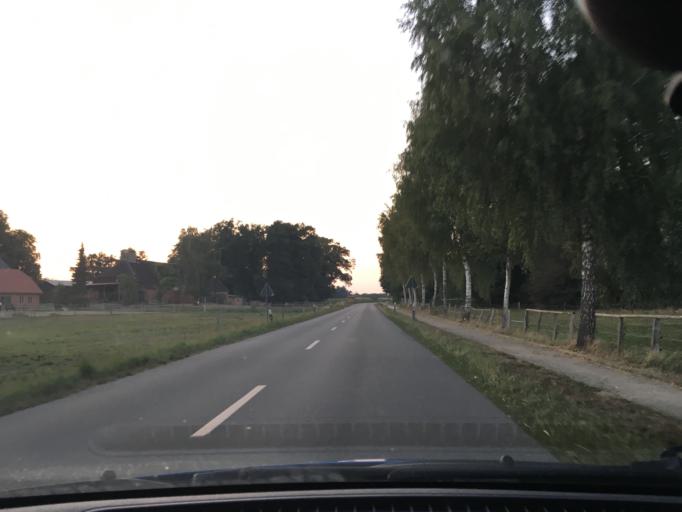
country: DE
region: Lower Saxony
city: Embsen
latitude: 53.1577
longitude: 10.3462
